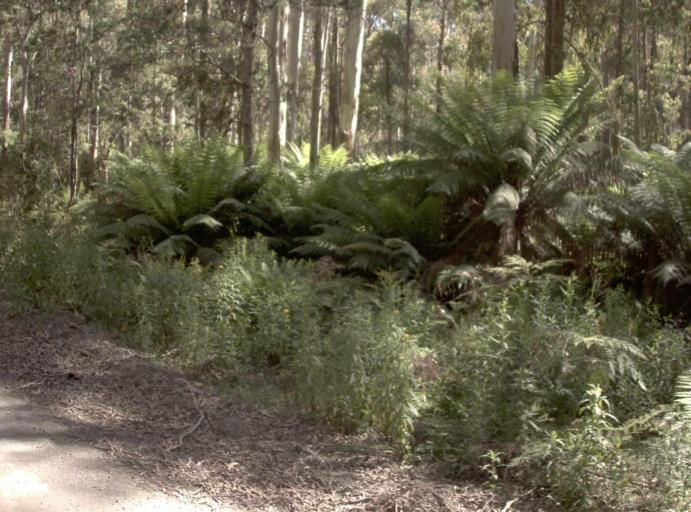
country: AU
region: New South Wales
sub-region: Bombala
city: Bombala
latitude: -37.2349
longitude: 148.7545
